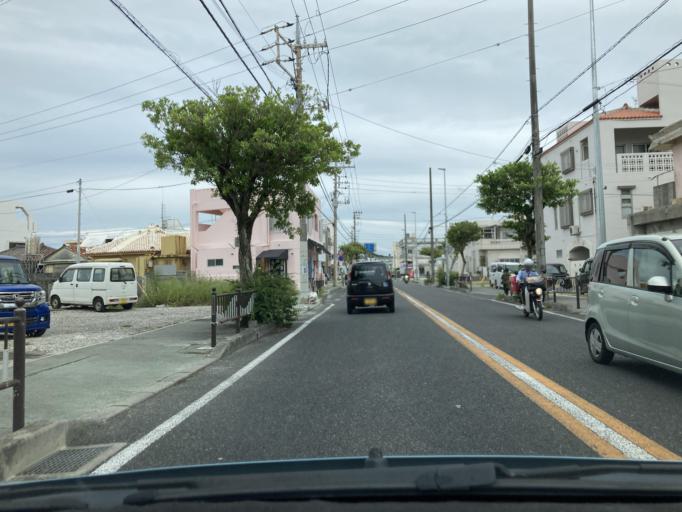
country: JP
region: Okinawa
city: Itoman
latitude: 26.1278
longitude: 127.6690
